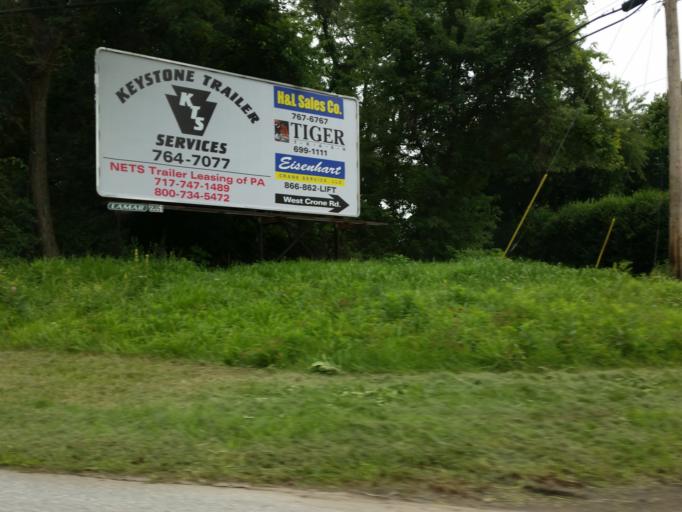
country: US
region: Pennsylvania
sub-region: York County
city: Emigsville
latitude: 40.0243
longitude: -76.7472
